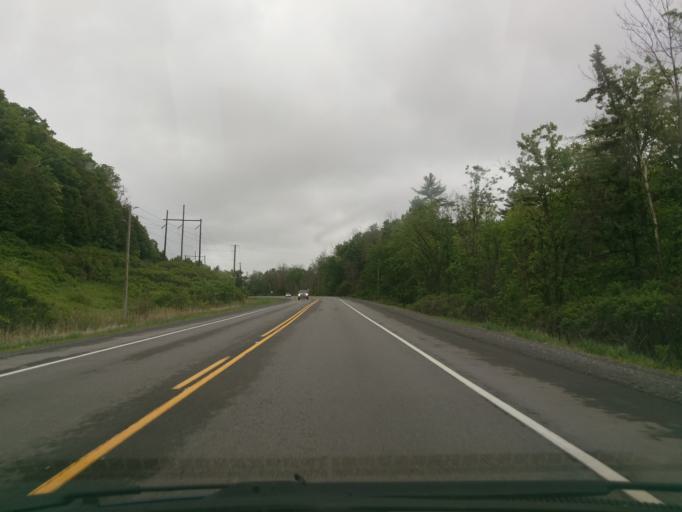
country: CA
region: Ontario
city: Clarence-Rockland
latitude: 45.5166
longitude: -75.4430
